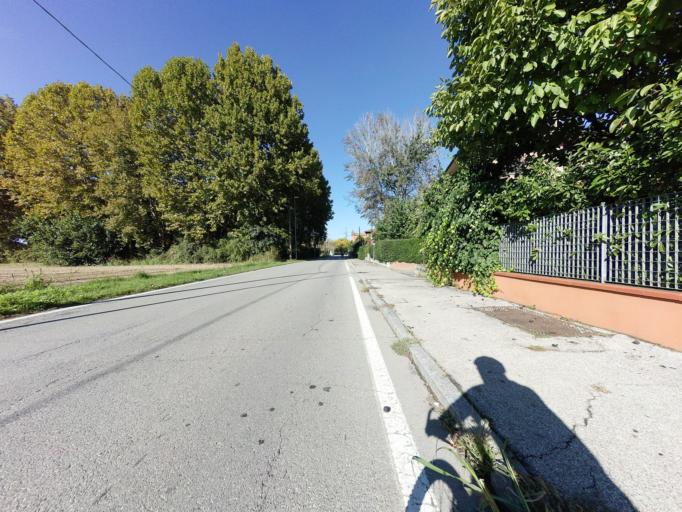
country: IT
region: Emilia-Romagna
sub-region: Provincia di Bologna
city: Progresso
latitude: 44.5699
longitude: 11.3912
